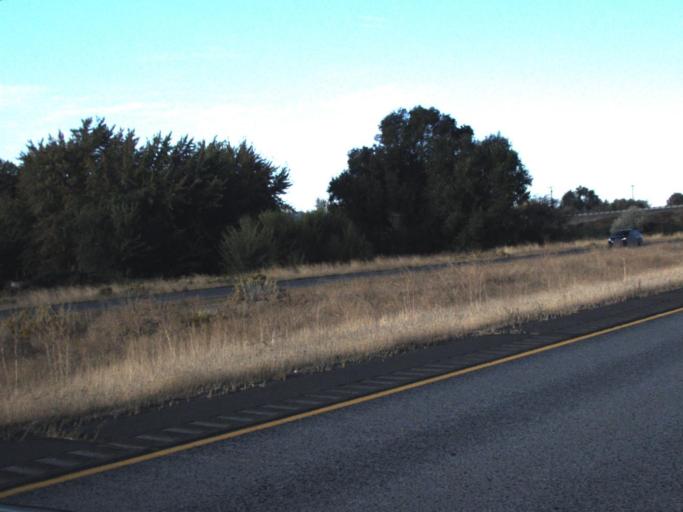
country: US
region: Washington
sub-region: Benton County
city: Prosser
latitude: 46.2214
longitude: -119.7639
